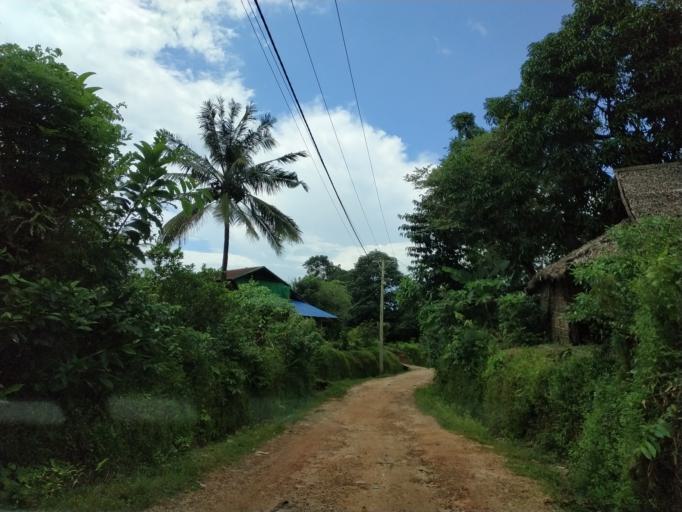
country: MM
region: Tanintharyi
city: Dawei
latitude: 14.1852
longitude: 98.1642
